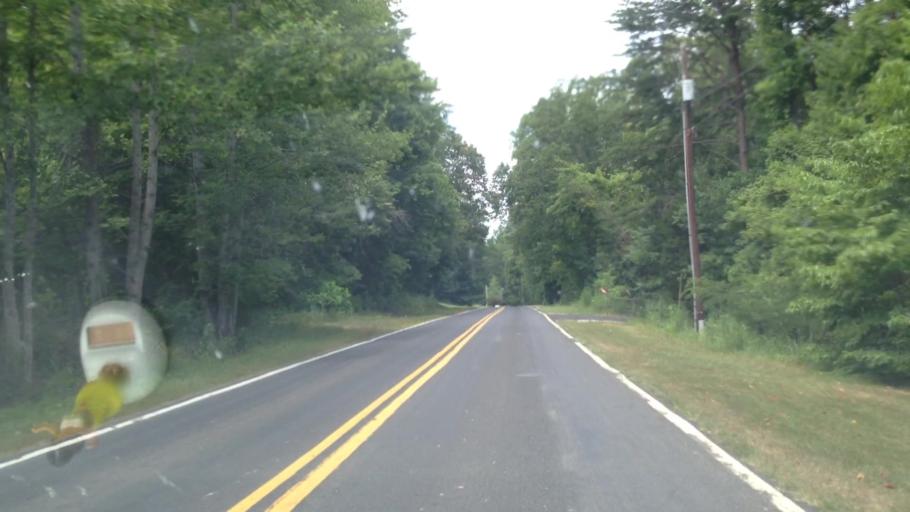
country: US
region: North Carolina
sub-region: Forsyth County
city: Walkertown
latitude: 36.2080
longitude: -80.1091
